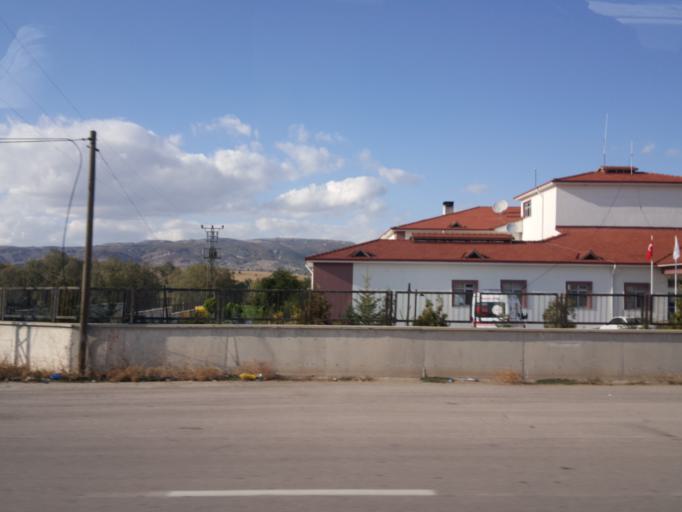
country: TR
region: Tokat
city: Yesilyurt
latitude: 40.0124
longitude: 36.2306
